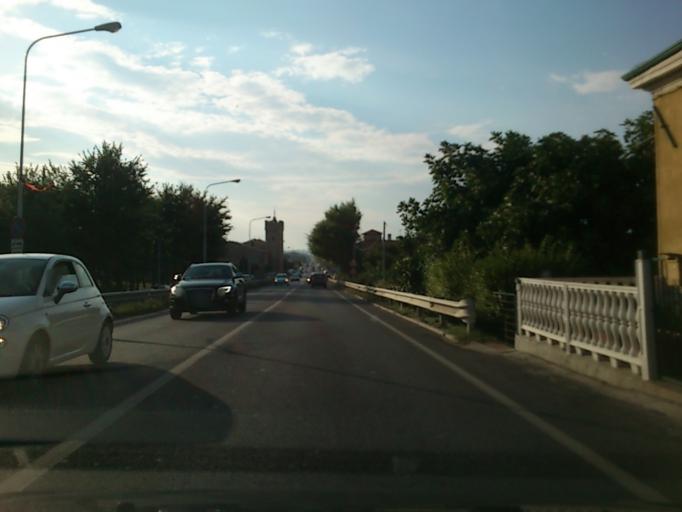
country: IT
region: The Marches
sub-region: Provincia di Pesaro e Urbino
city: Fano
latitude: 43.8280
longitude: 13.0510
